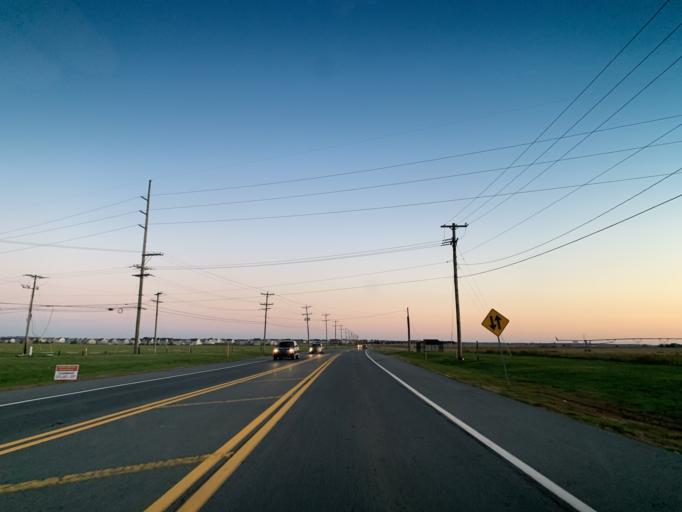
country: US
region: Delaware
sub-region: New Castle County
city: Middletown
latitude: 39.4373
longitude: -75.7452
